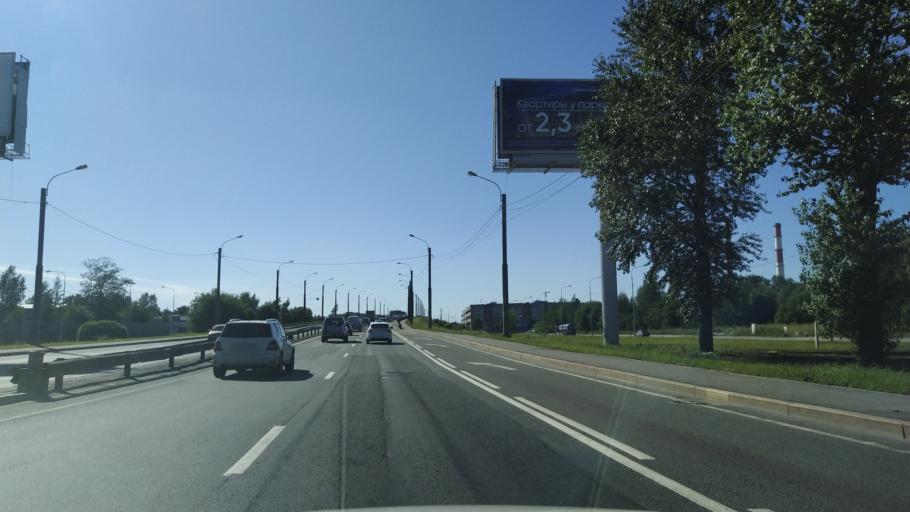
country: RU
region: St.-Petersburg
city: Krasnogvargeisky
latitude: 59.9895
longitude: 30.4507
